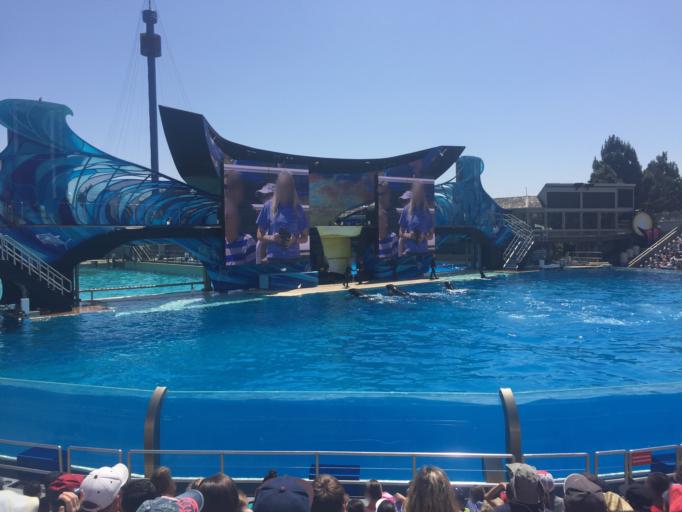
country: US
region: California
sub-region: San Diego County
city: San Diego
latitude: 32.7646
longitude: -117.2289
